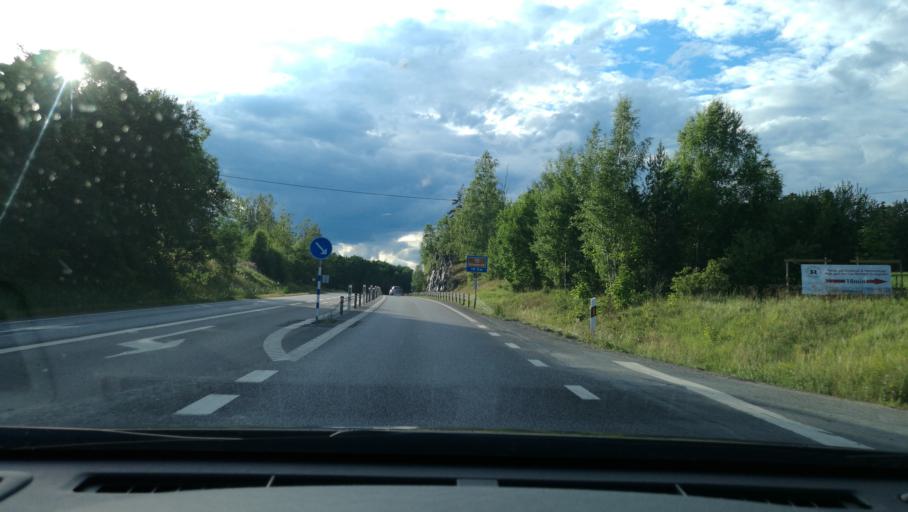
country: SE
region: OEstergoetland
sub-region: Norrkopings Kommun
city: Svartinge
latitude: 58.6854
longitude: 15.9350
